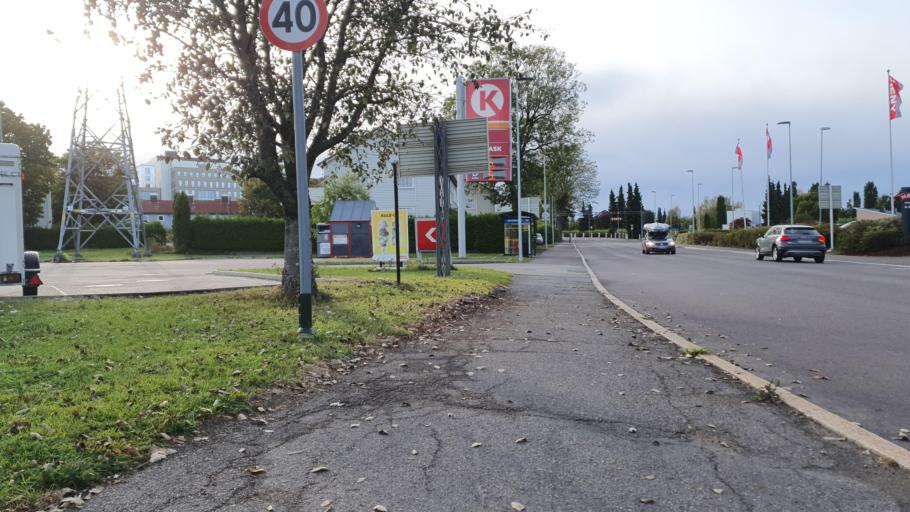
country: NO
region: Vestfold
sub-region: Tonsberg
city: Tonsberg
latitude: 59.2736
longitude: 10.4261
